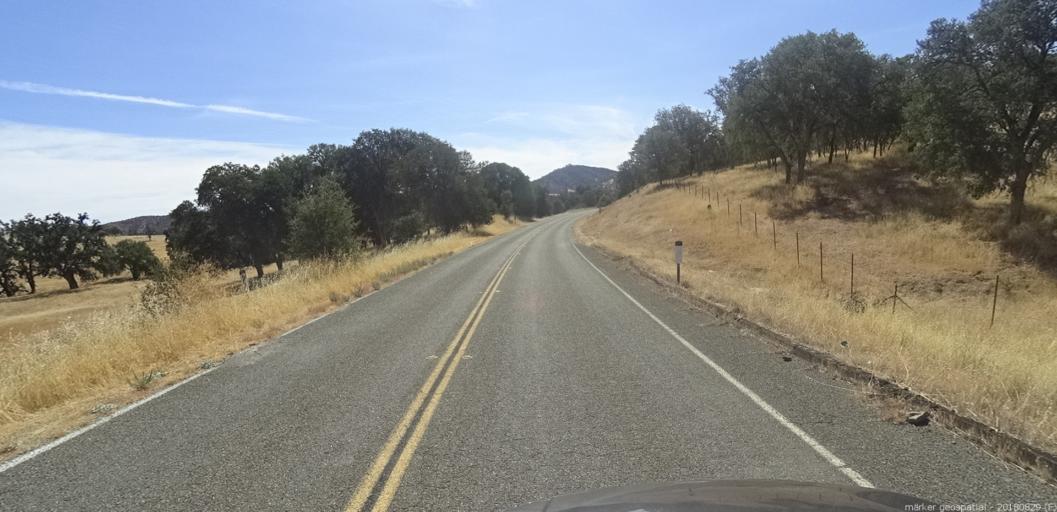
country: US
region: California
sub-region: San Luis Obispo County
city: Lake Nacimiento
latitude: 35.8082
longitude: -120.9970
